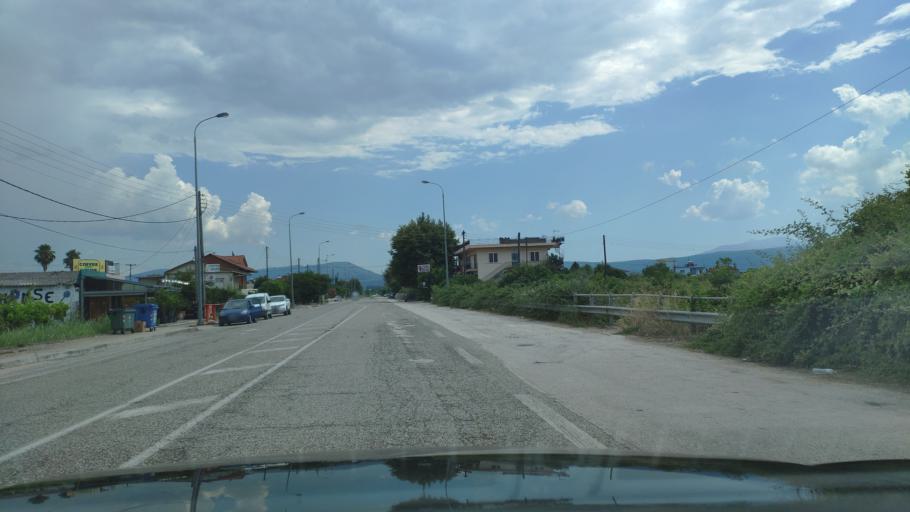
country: GR
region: West Greece
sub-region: Nomos Aitolias kai Akarnanias
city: Krikellos
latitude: 38.9499
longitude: 21.1761
